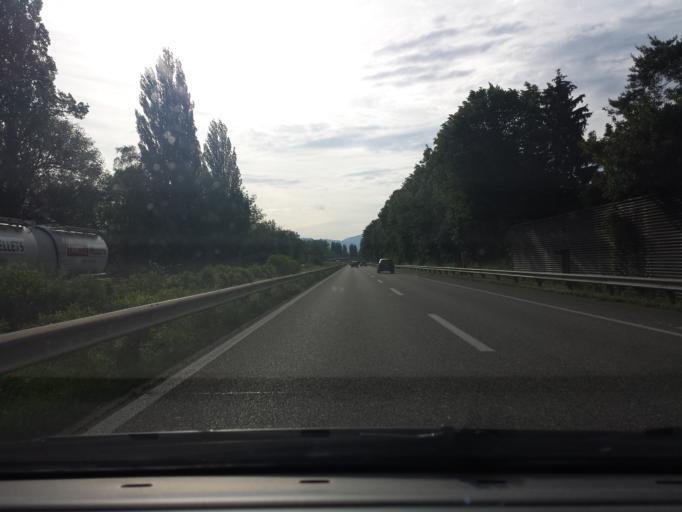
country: CH
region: Saint Gallen
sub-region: Wahlkreis Rheintal
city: Sankt Margrethen
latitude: 47.4561
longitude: 9.6310
